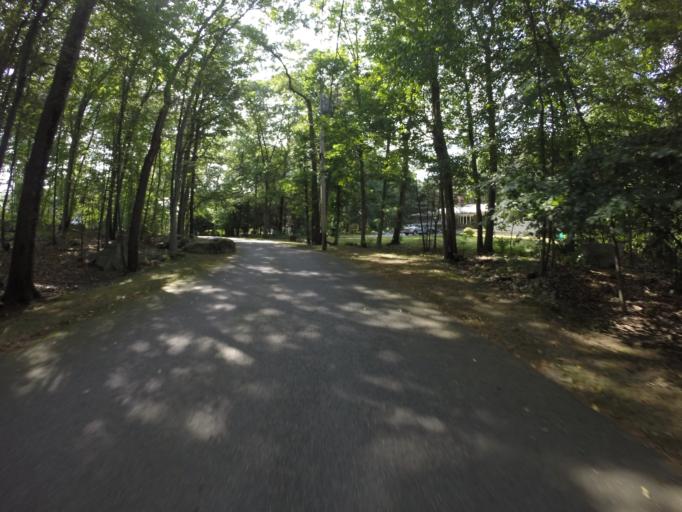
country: US
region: Massachusetts
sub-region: Norfolk County
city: Stoughton
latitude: 42.0811
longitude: -71.1129
